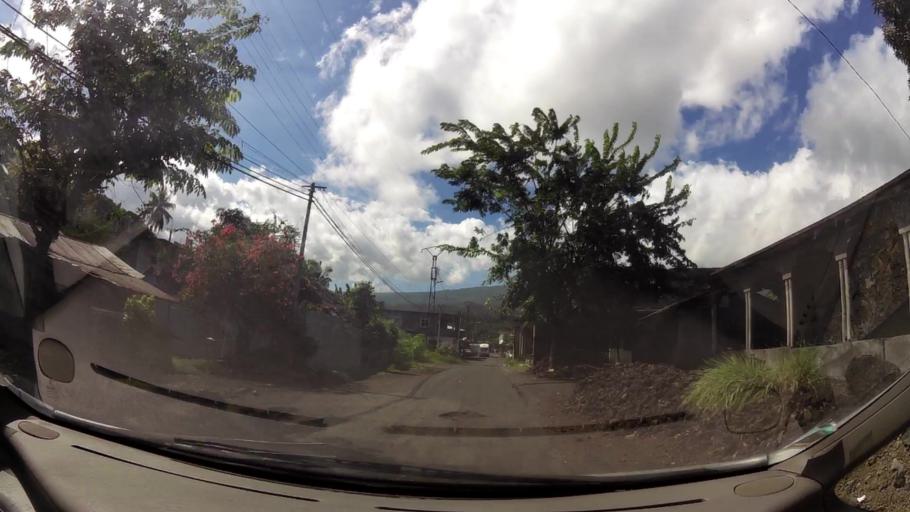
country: KM
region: Grande Comore
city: Mavingouni
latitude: -11.7394
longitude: 43.2481
